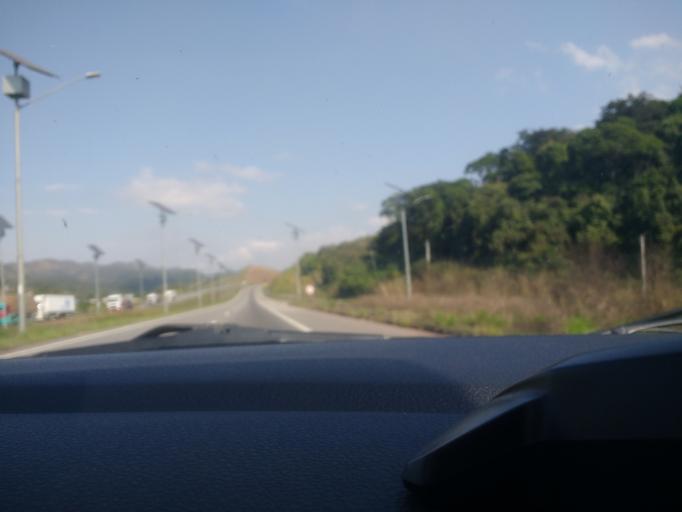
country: BR
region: Rio de Janeiro
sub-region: Nova Iguacu
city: Nova Iguacu
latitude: -22.6843
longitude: -43.4791
